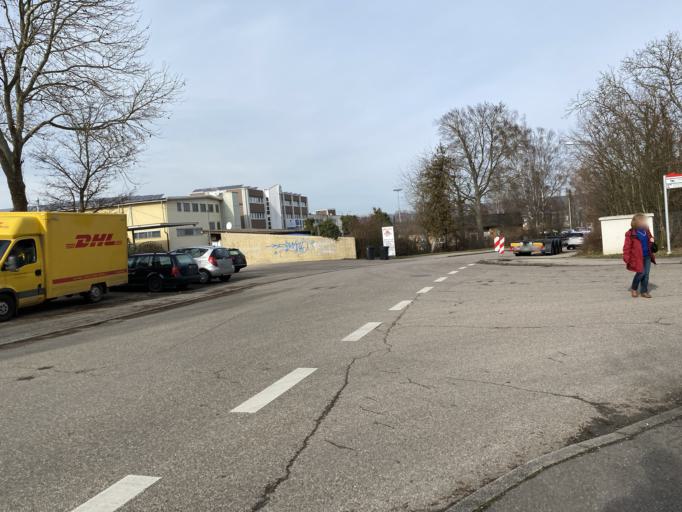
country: DE
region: Baden-Wuerttemberg
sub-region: Regierungsbezirk Stuttgart
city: Vaihingen an der Enz
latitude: 48.9403
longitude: 8.9559
